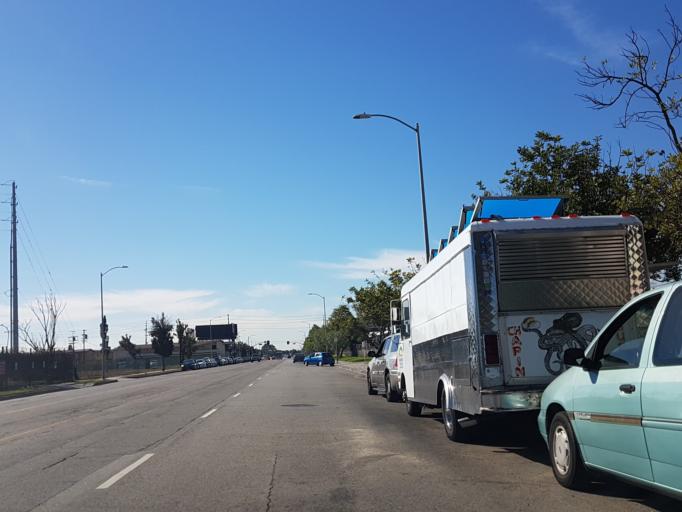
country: US
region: California
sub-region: Los Angeles County
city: Inglewood
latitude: 33.9527
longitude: -118.3827
